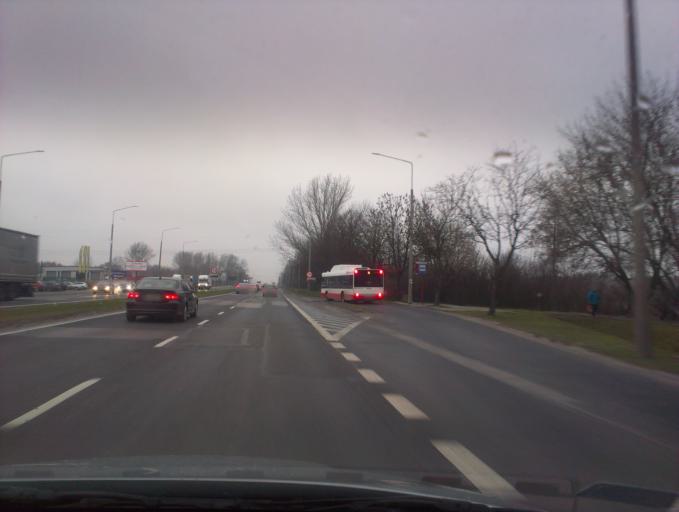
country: PL
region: Masovian Voivodeship
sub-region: Radom
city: Radom
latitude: 51.4533
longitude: 21.1422
